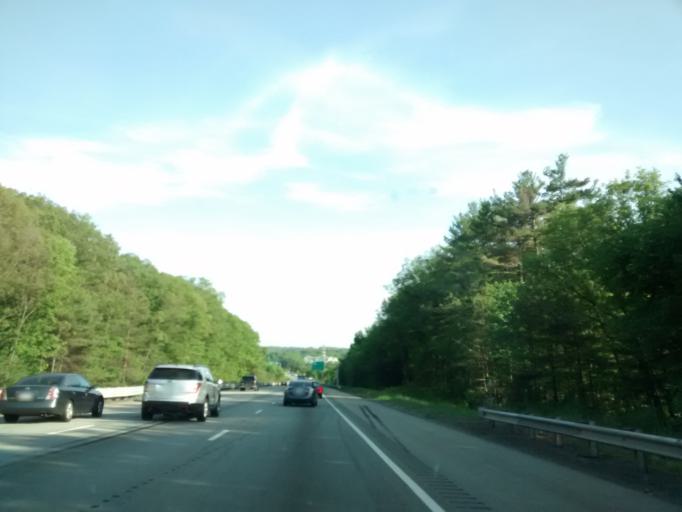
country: US
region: Massachusetts
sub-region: Middlesex County
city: Hudson
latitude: 42.3735
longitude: -71.5979
